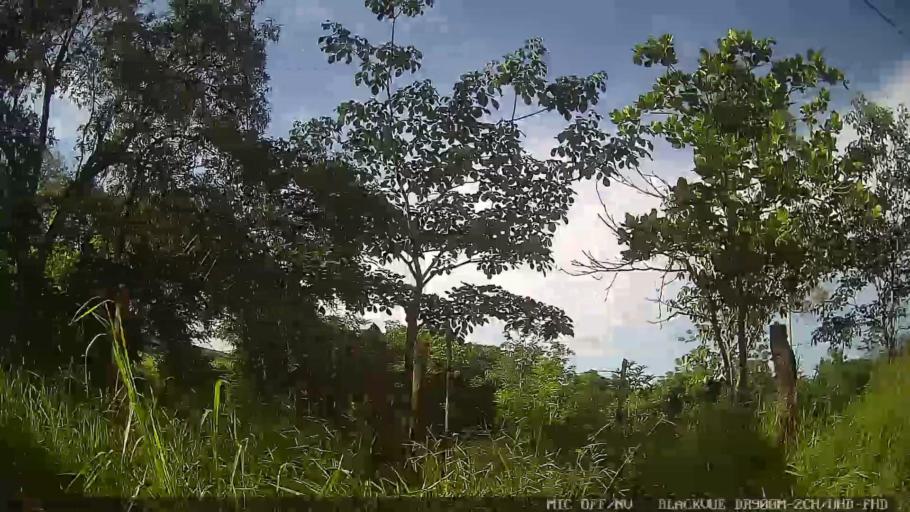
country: BR
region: Sao Paulo
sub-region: Tiete
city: Tiete
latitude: -23.0859
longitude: -47.6925
